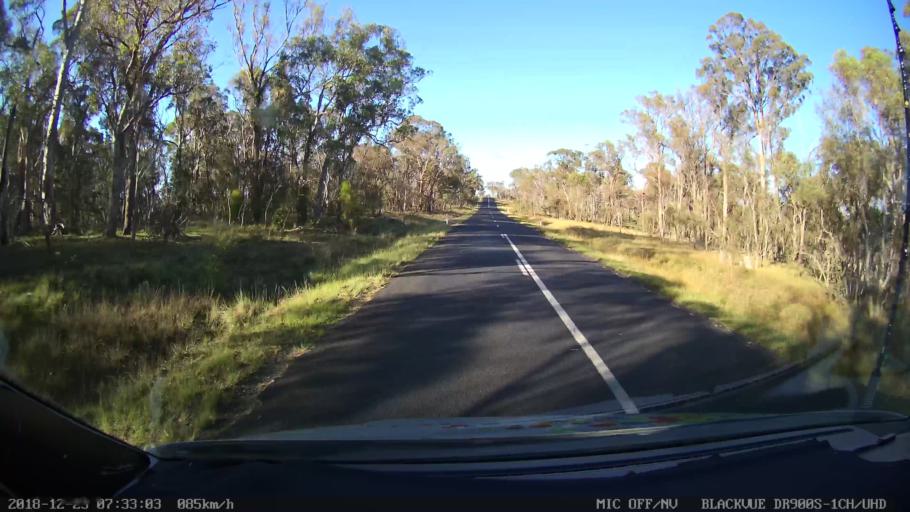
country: AU
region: New South Wales
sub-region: Armidale Dumaresq
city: Enmore
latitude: -30.5091
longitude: 152.1088
